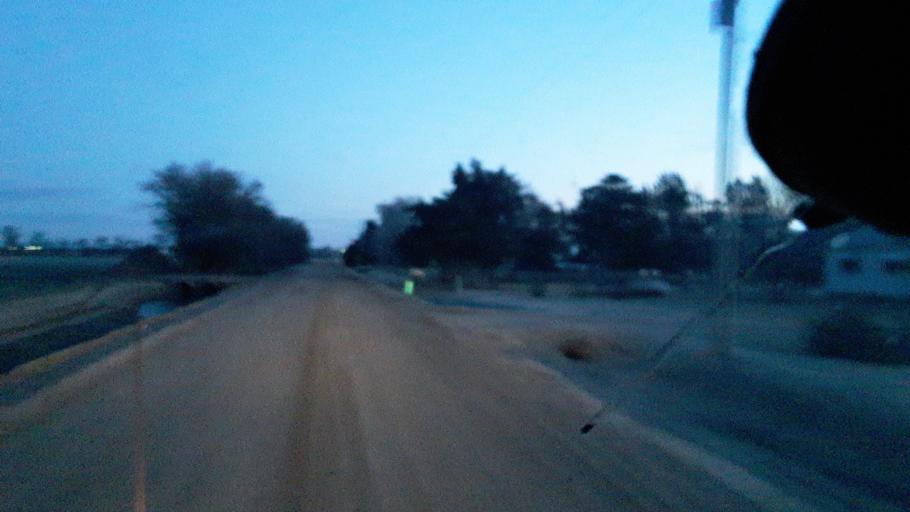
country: US
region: Kansas
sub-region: Reno County
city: South Hutchinson
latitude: 37.9887
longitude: -97.9770
